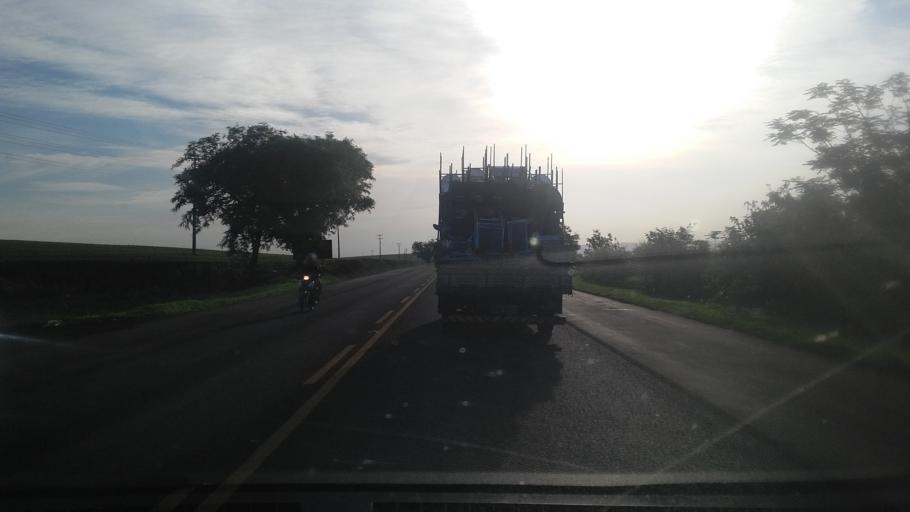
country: BR
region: Parana
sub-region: Bandeirantes
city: Bandeirantes
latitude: -23.1472
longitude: -50.5565
